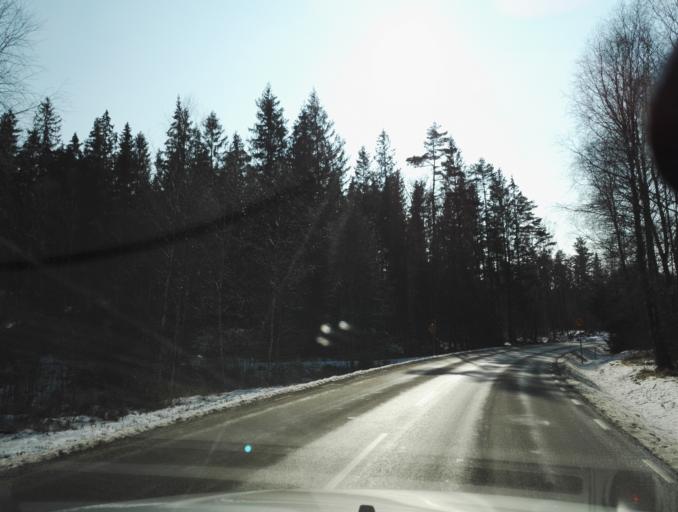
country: SE
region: Vaestra Goetaland
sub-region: Bollebygds Kommun
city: Bollebygd
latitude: 57.7079
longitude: 12.5827
